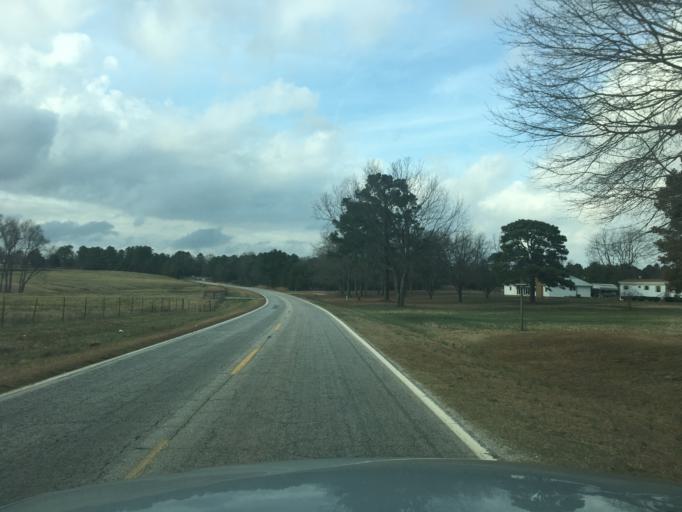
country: US
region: South Carolina
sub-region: Abbeville County
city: Abbeville
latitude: 34.2331
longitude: -82.3931
